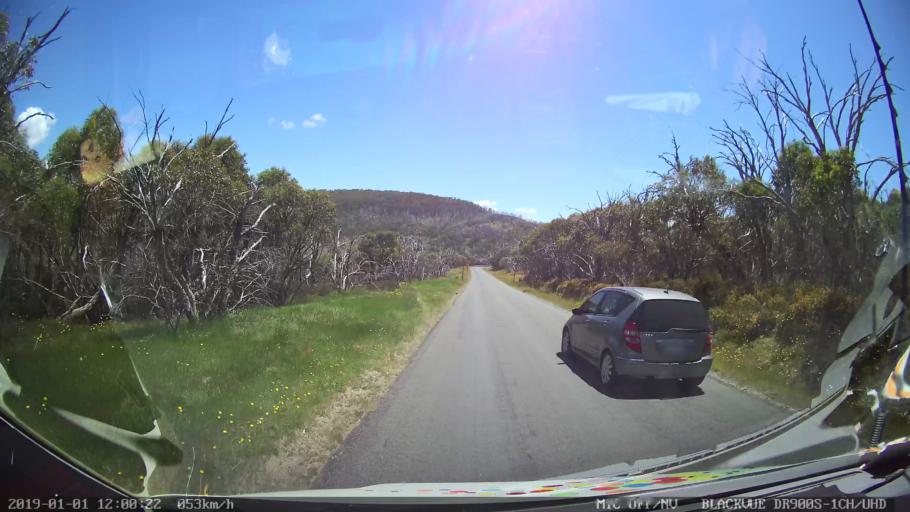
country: AU
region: New South Wales
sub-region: Snowy River
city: Jindabyne
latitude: -35.8854
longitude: 148.4591
